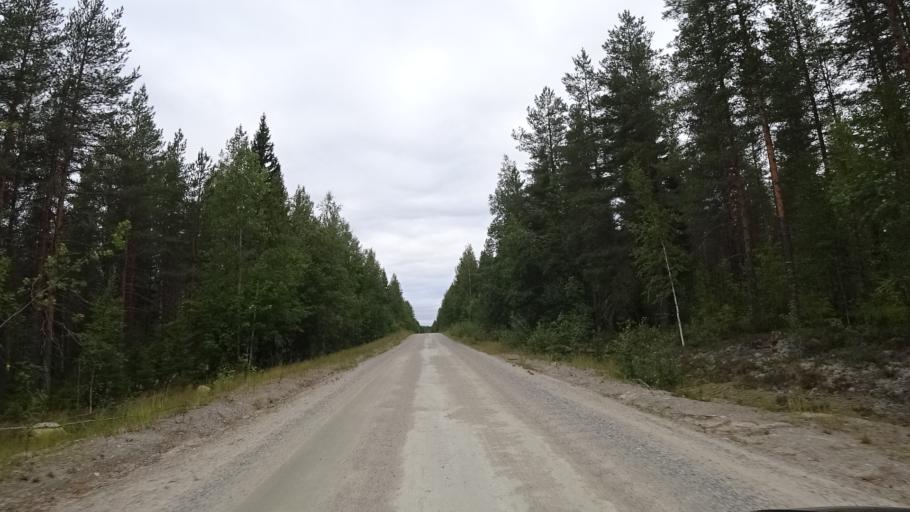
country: FI
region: North Karelia
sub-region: Joensuu
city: Eno
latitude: 63.1549
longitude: 30.6077
